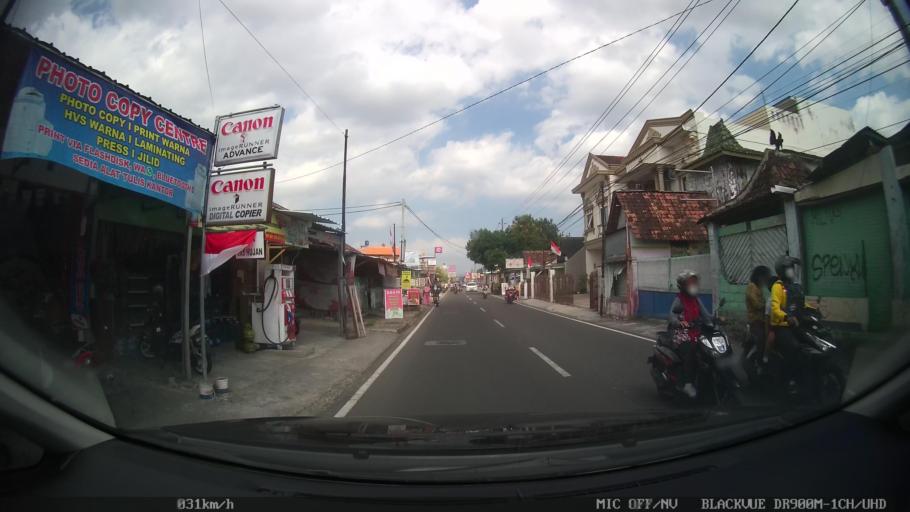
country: ID
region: Daerah Istimewa Yogyakarta
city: Yogyakarta
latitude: -7.7696
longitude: 110.3568
